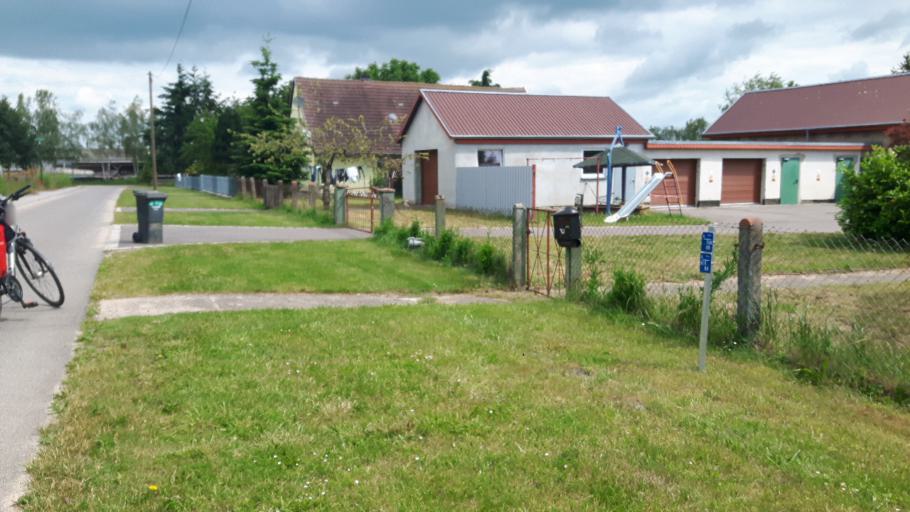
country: DE
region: Brandenburg
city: Mescherin
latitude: 53.2827
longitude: 14.4090
